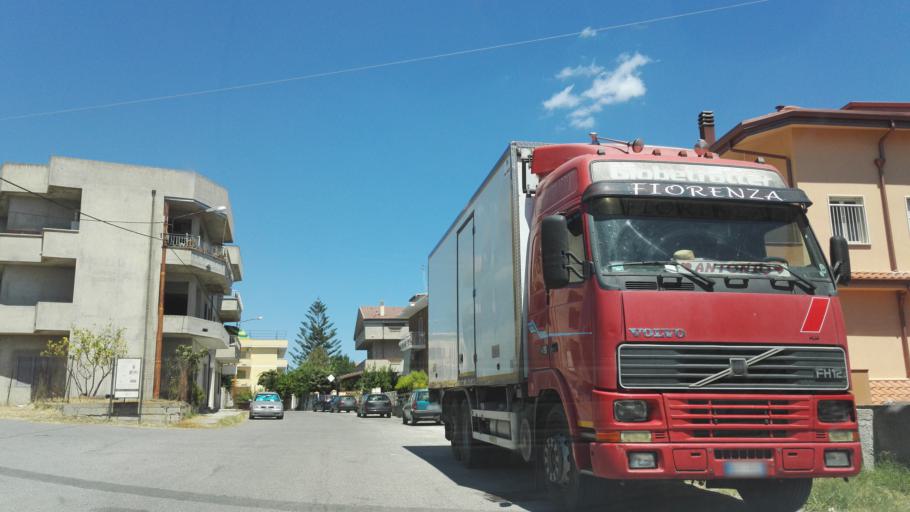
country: IT
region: Calabria
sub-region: Provincia di Reggio Calabria
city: Monasterace Marina
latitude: 38.4368
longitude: 16.5718
